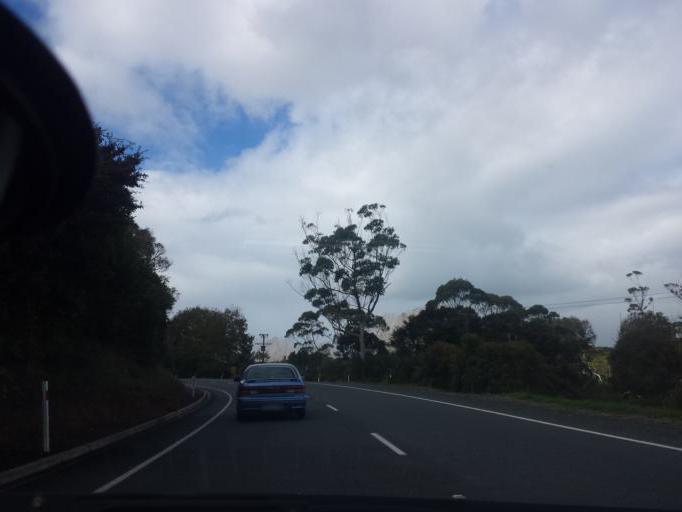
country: NZ
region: Auckland
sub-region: Auckland
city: Warkworth
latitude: -36.3986
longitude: 174.7029
